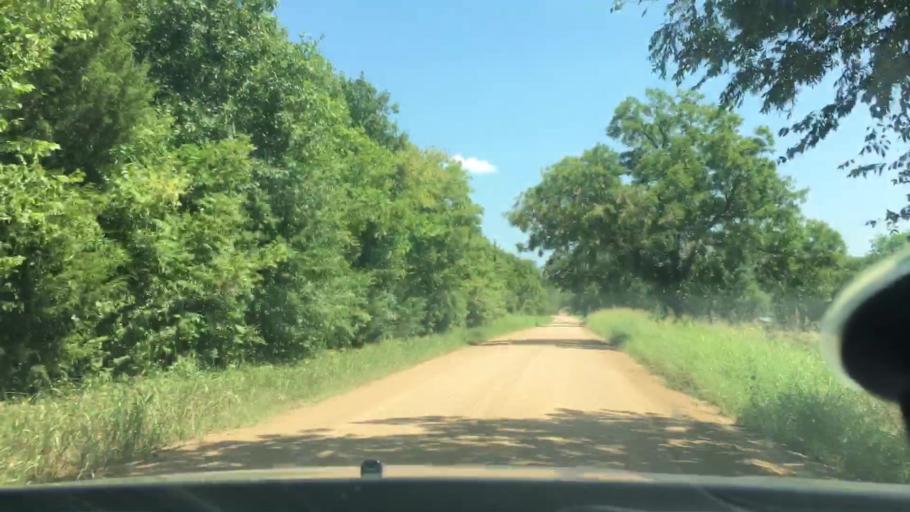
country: US
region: Oklahoma
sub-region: Coal County
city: Coalgate
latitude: 34.3681
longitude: -96.4317
